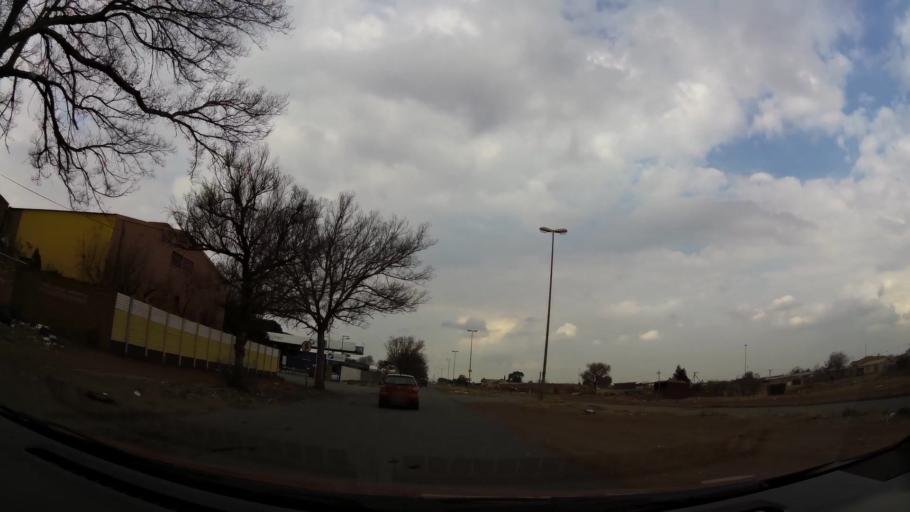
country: ZA
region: Gauteng
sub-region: Sedibeng District Municipality
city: Vanderbijlpark
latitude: -26.6605
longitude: 27.8475
